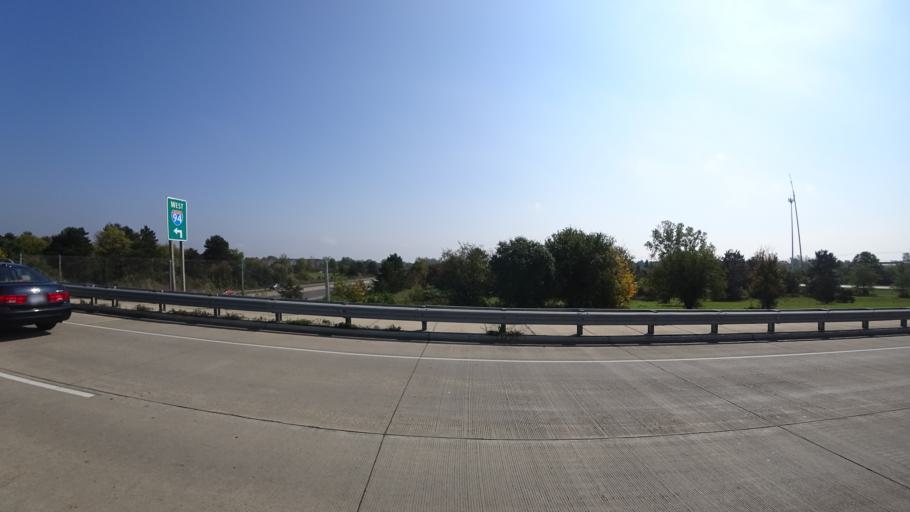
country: US
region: Michigan
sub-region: Washtenaw County
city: Ann Arbor
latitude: 42.2451
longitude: -83.7640
